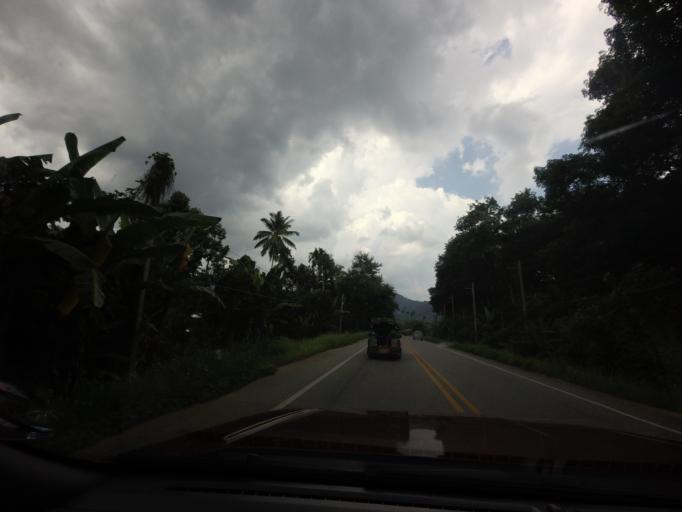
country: TH
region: Yala
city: Than To
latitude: 6.2350
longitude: 101.1678
